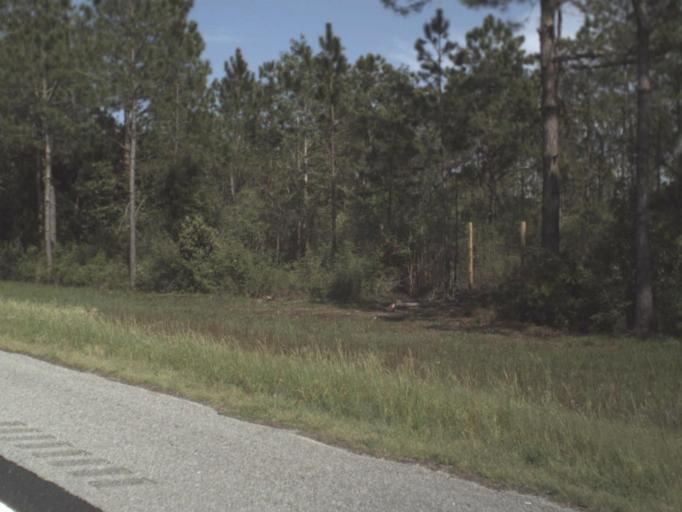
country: US
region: Florida
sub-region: Santa Rosa County
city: Bagdad
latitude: 30.5536
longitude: -87.0524
